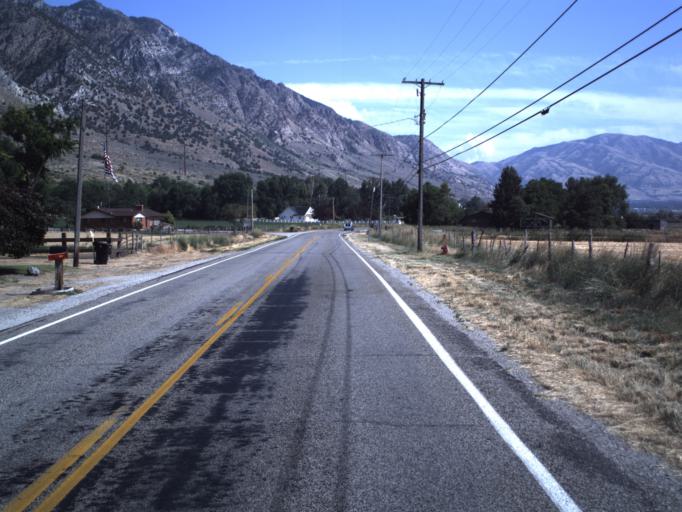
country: US
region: Utah
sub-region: Box Elder County
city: Honeyville
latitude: 41.5849
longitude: -112.0392
